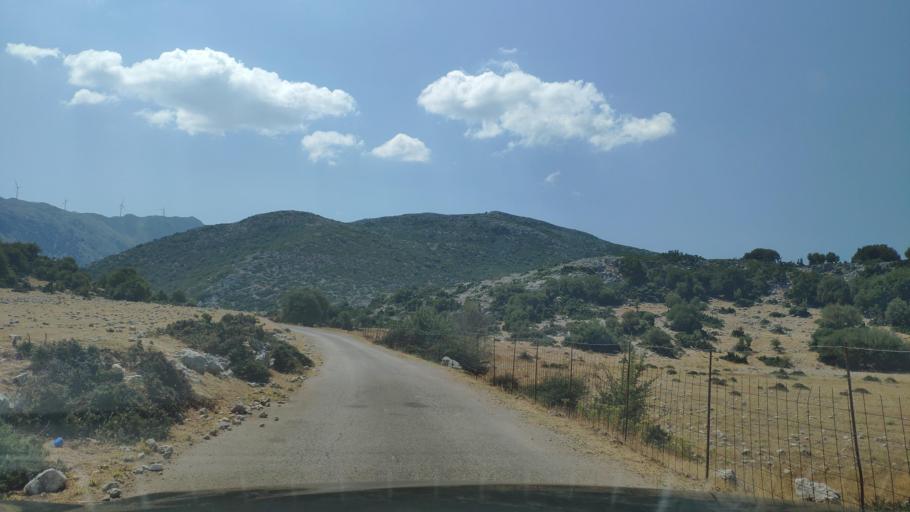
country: GR
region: West Greece
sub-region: Nomos Aitolias kai Akarnanias
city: Monastirakion
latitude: 38.8006
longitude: 20.9483
